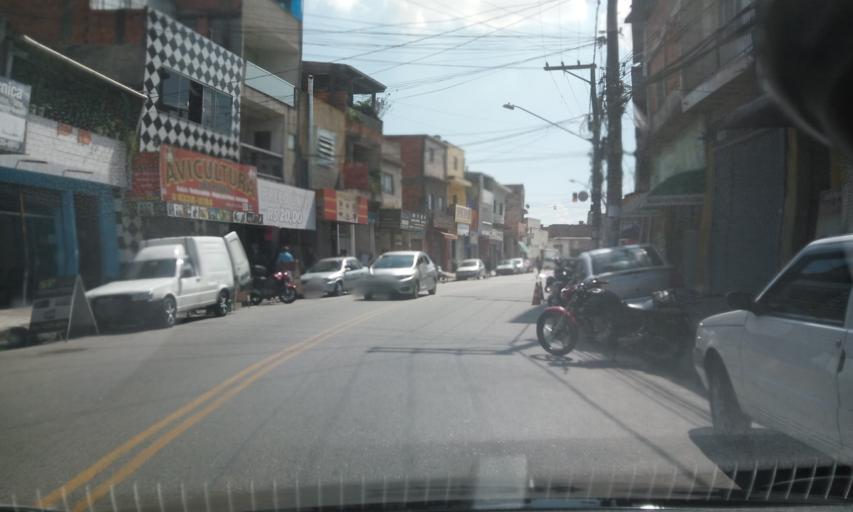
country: BR
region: Sao Paulo
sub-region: Sao Bernardo Do Campo
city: Sao Bernardo do Campo
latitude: -23.7169
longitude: -46.5291
